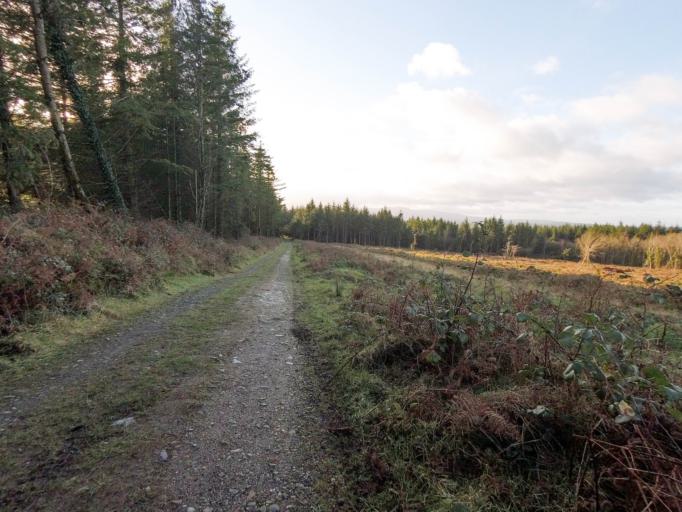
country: IE
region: Munster
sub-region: Waterford
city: Portlaw
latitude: 52.3117
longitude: -7.3516
